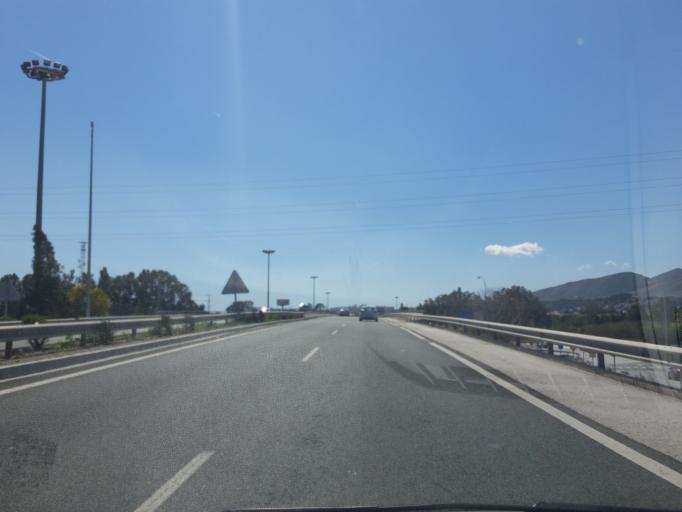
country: ES
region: Andalusia
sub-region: Provincia de Malaga
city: Torremolinos
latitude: 36.6542
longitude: -4.4779
